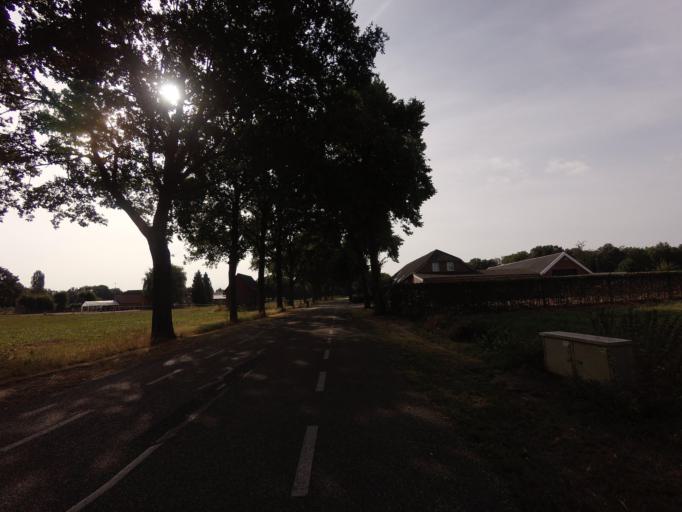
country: NL
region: North Brabant
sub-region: Gemeente Mill en Sint Hubert
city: Wilbertoord
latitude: 51.6457
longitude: 5.8142
